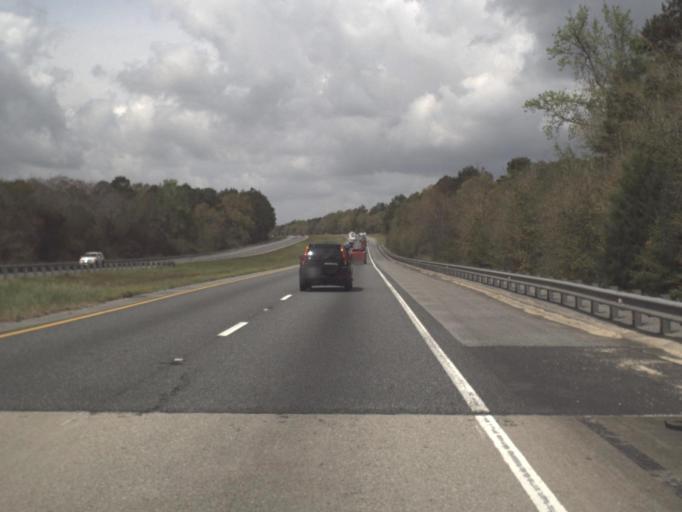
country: US
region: Florida
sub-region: Okaloosa County
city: Crestview
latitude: 30.7165
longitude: -86.6505
